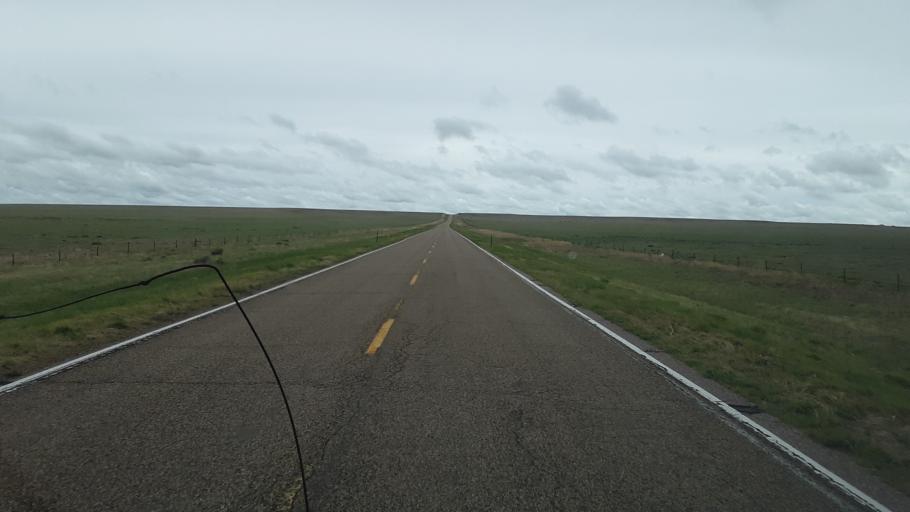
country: US
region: Colorado
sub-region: Lincoln County
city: Hugo
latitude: 38.8498
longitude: -103.3786
